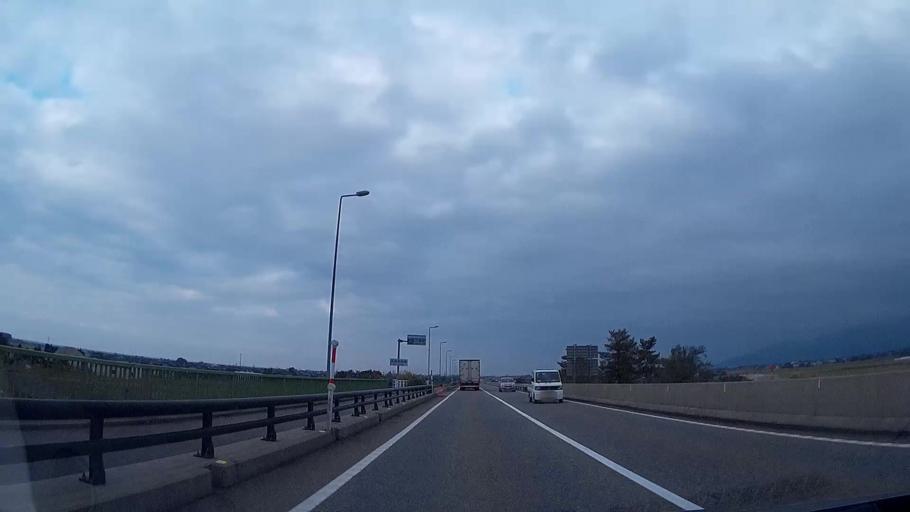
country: JP
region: Toyama
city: Nyuzen
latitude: 36.9068
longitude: 137.4525
